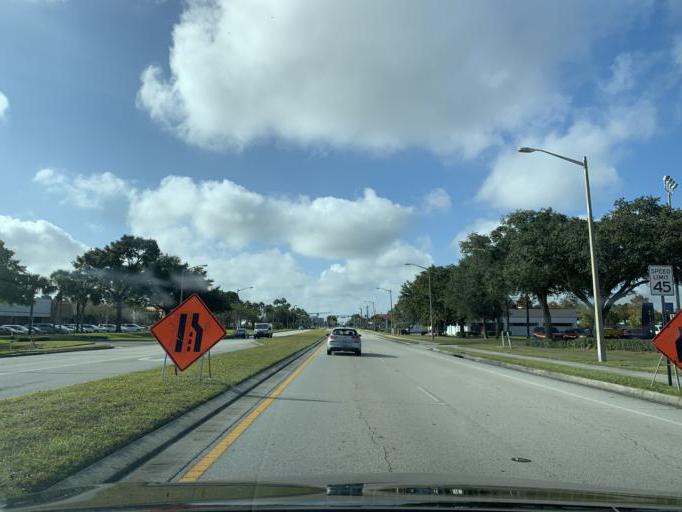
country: US
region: Florida
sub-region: Orange County
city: Oak Ridge
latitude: 28.4991
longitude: -81.4324
